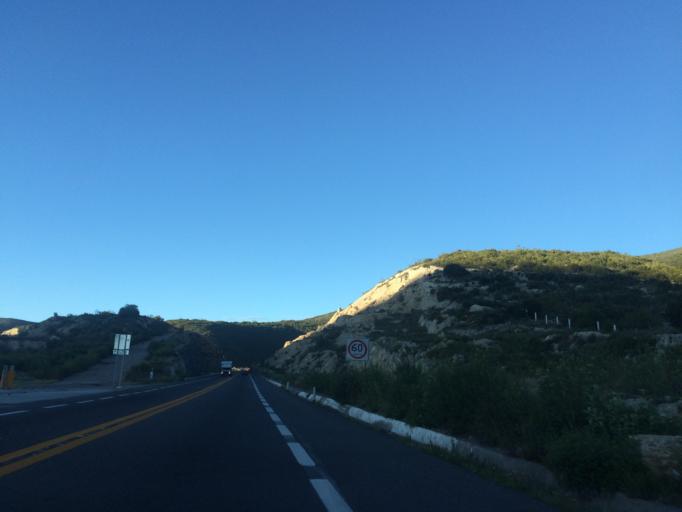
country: MX
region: Puebla
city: Chapuco
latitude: 18.6645
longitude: -97.4564
